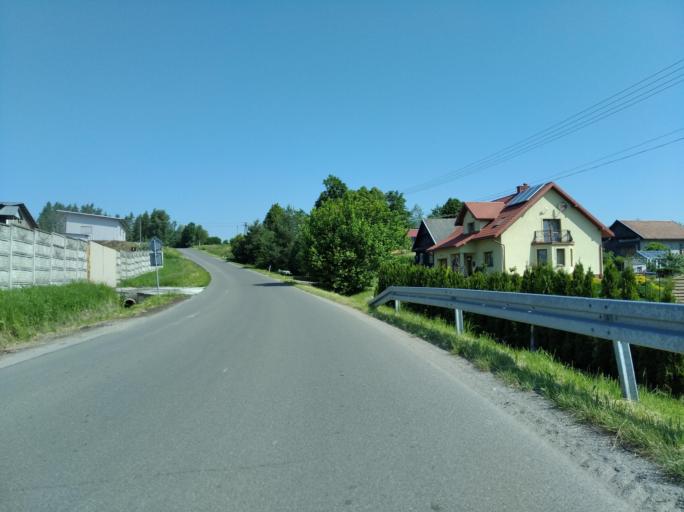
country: PL
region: Subcarpathian Voivodeship
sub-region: Powiat ropczycko-sedziszowski
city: Wielopole Skrzynskie
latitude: 49.9495
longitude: 21.6214
